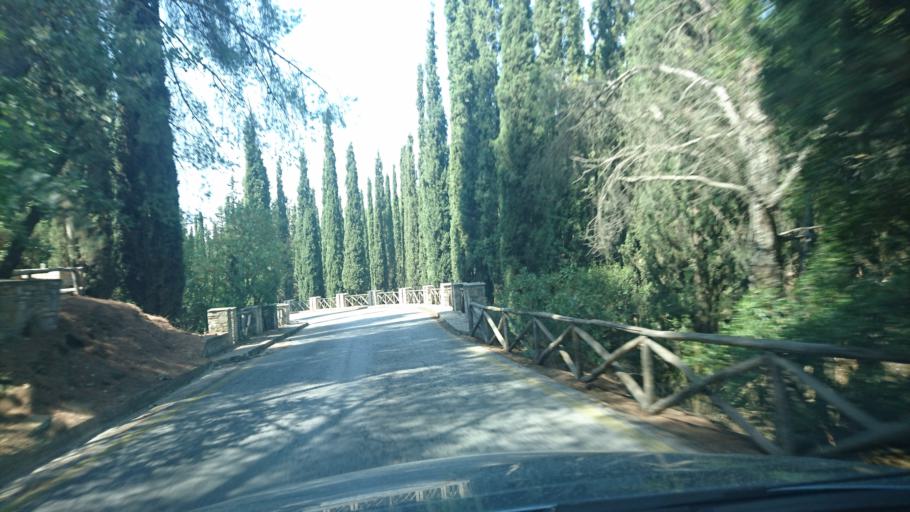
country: GR
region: Attica
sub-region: Nomos Attikis
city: Zografos
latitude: 37.9632
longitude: 23.7957
